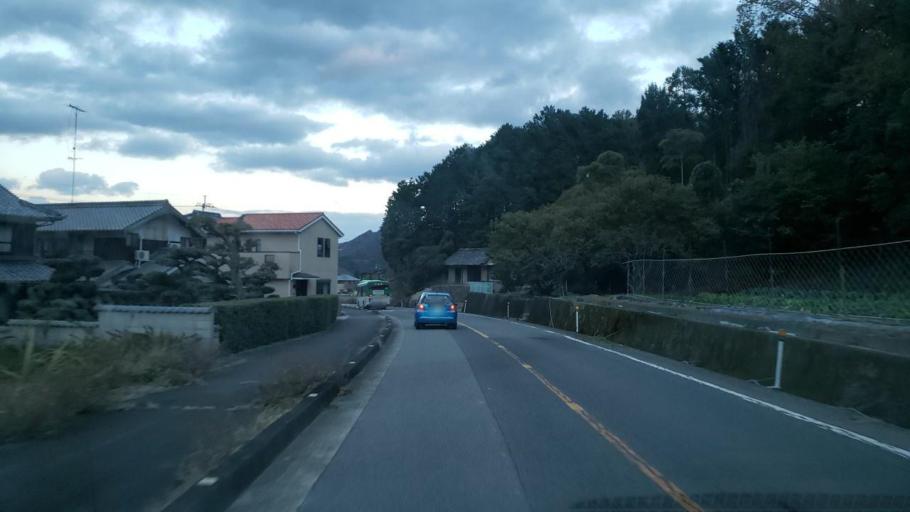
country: JP
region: Tokushima
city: Kamojimacho-jogejima
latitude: 34.2069
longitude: 134.3272
